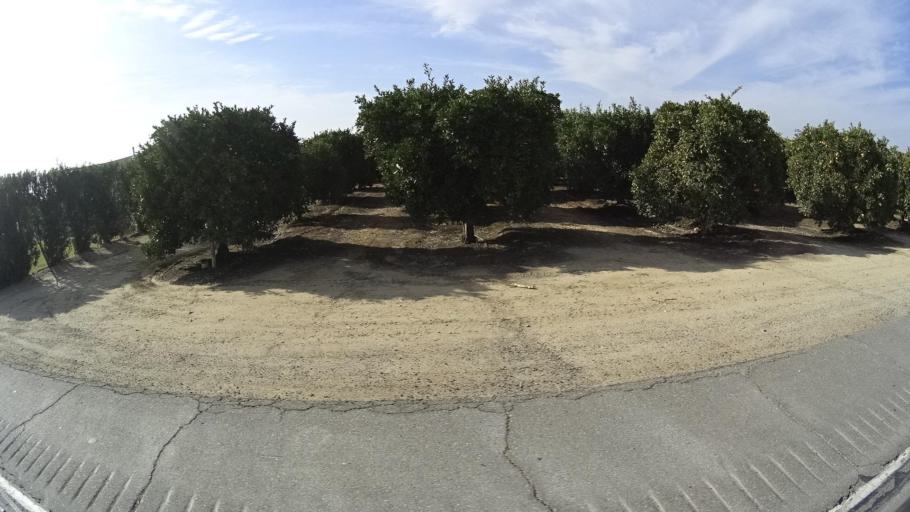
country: US
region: California
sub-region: Kern County
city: Lamont
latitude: 35.3200
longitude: -118.8431
